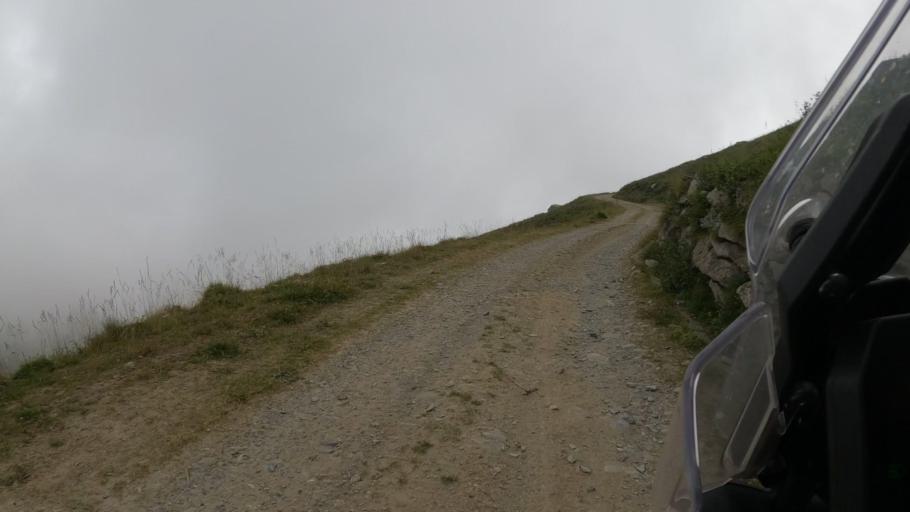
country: IT
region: Piedmont
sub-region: Provincia di Torino
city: Lemie
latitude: 45.1806
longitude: 7.2818
